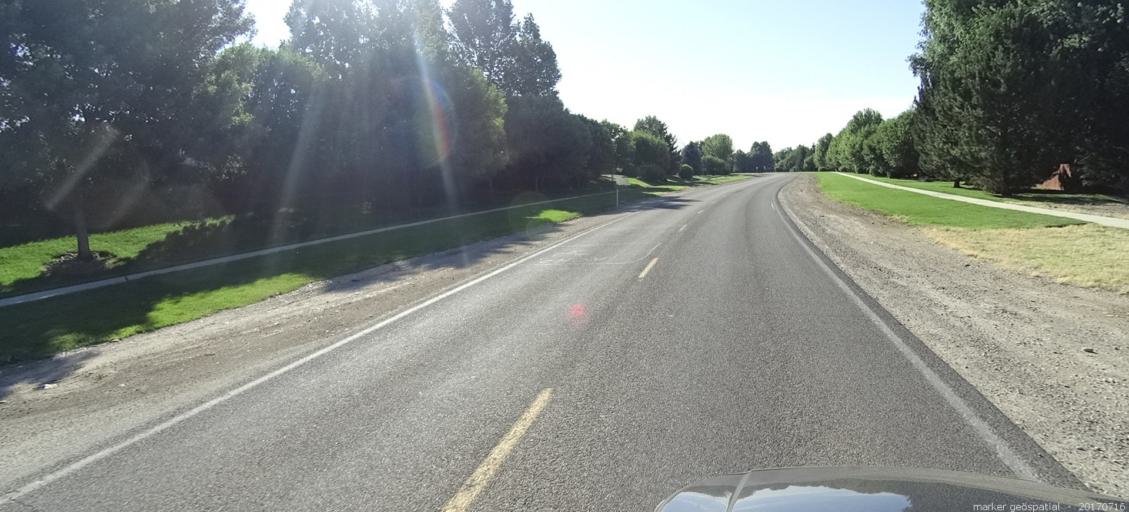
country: US
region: Idaho
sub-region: Ada County
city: Garden City
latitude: 43.5461
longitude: -116.2888
